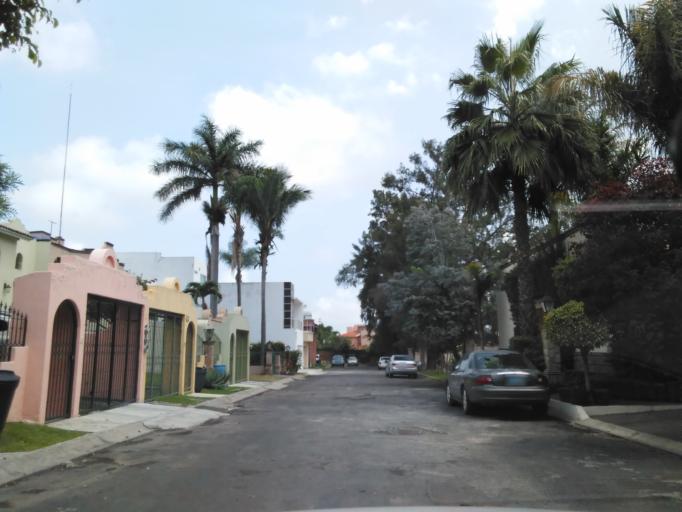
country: MX
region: Nayarit
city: Tepic
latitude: 21.5141
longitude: -104.9224
